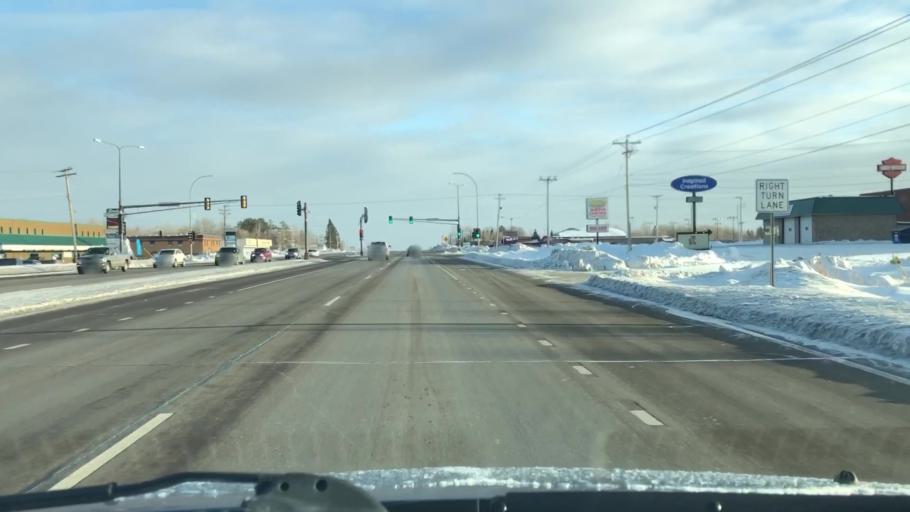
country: US
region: Minnesota
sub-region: Saint Louis County
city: Hermantown
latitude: 46.8283
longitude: -92.1969
